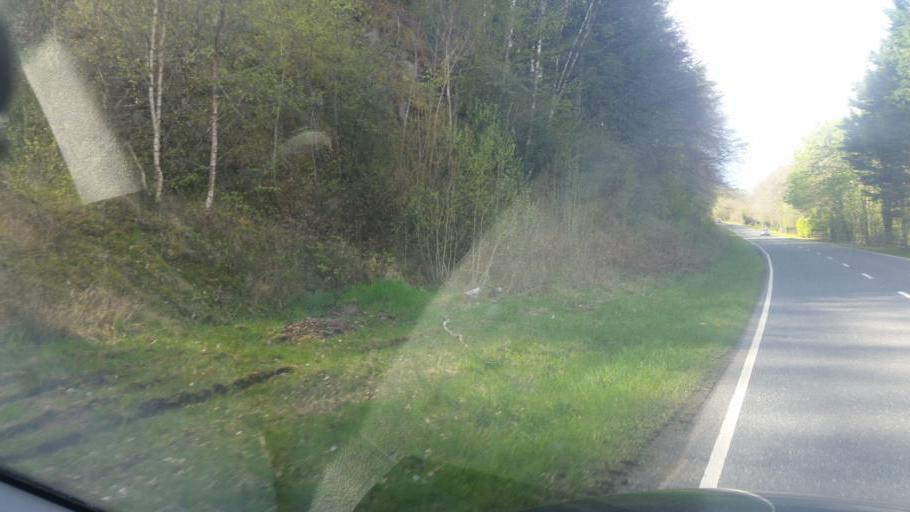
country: GB
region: Northern Ireland
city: Irvinestown
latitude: 54.4185
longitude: -7.7336
